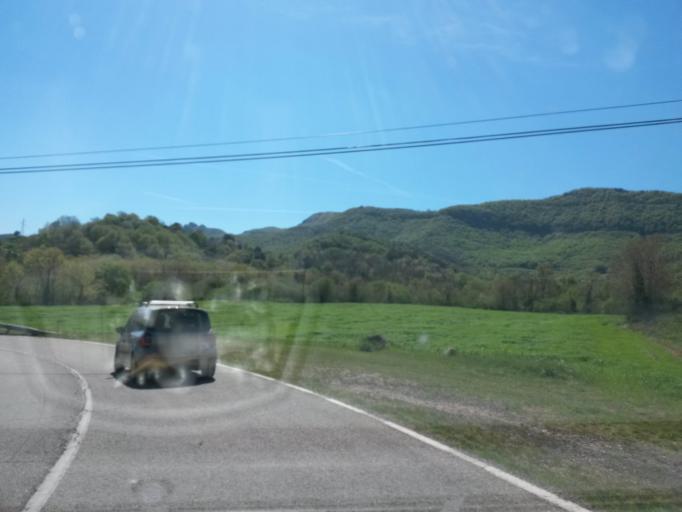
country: ES
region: Catalonia
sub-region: Provincia de Girona
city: Santa Pau
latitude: 42.1451
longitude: 2.5632
